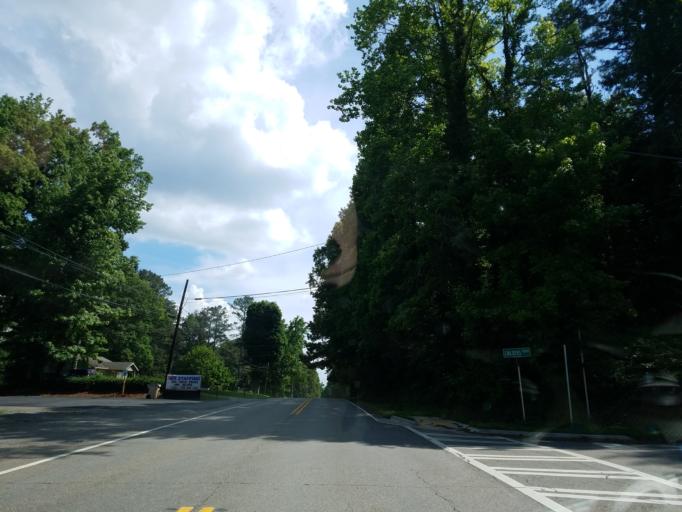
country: US
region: Georgia
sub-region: Cherokee County
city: Holly Springs
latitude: 34.1682
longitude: -84.5049
